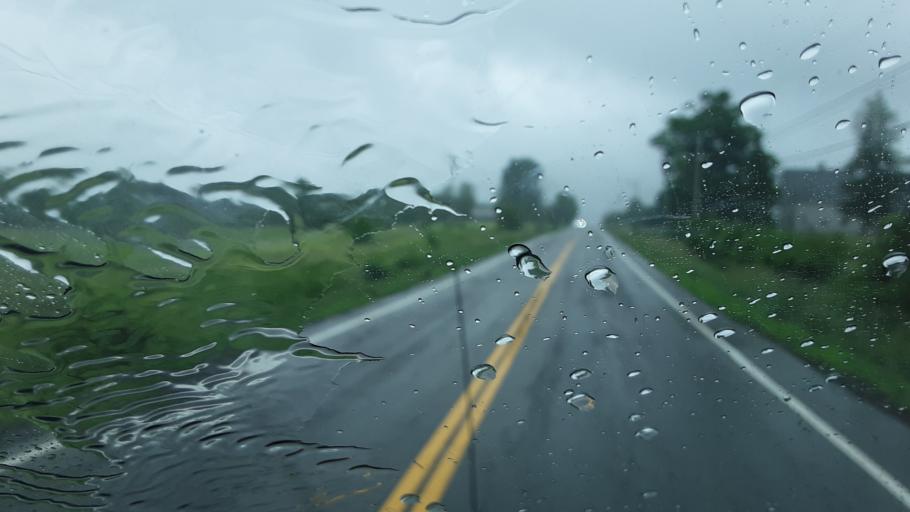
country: US
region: Maine
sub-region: Penobscot County
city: Patten
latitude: 46.0238
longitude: -68.4453
